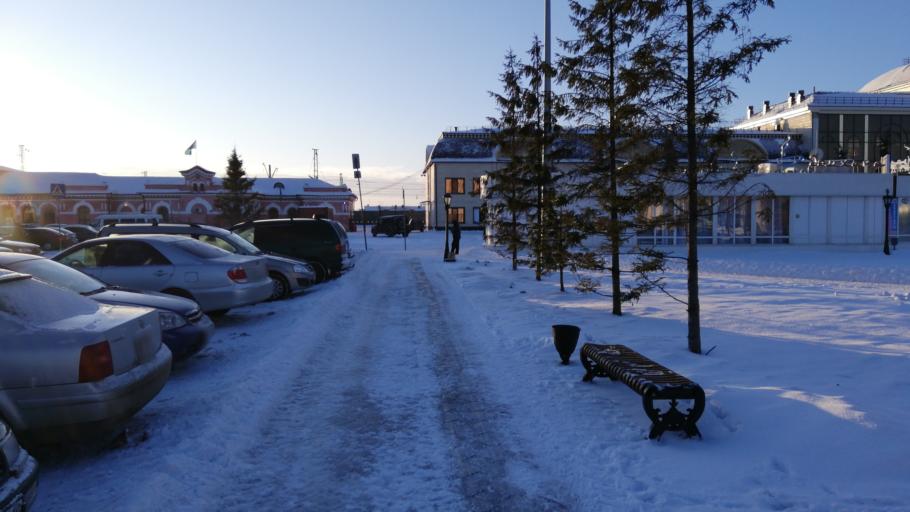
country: KZ
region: Soltustik Qazaqstan
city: Petropavlovsk
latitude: 54.8573
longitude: 69.1712
